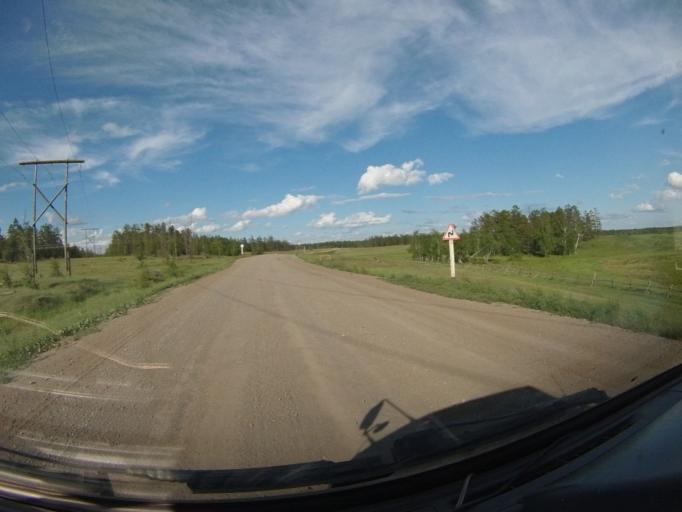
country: RU
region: Sakha
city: Ytyk-Kyuyel'
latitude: 62.2209
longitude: 133.2718
